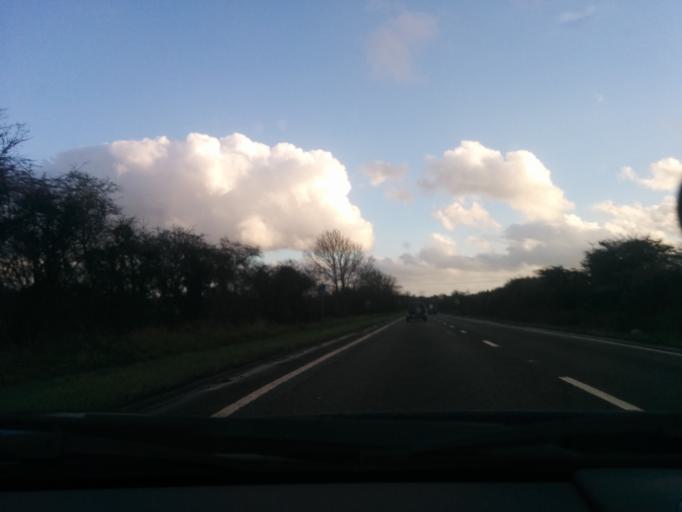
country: GB
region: England
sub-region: Oxfordshire
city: Oxford
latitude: 51.7414
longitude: -1.2795
